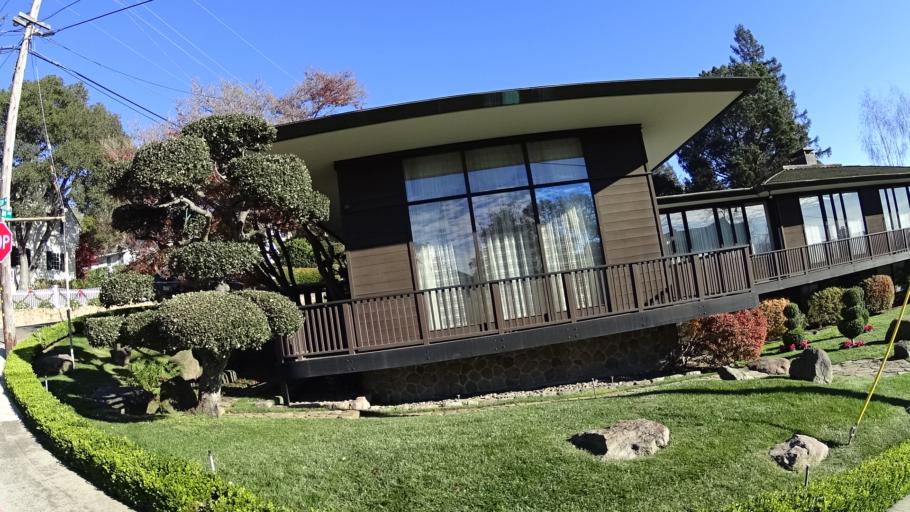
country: US
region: California
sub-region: Alameda County
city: Piedmont
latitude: 37.8231
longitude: -122.2269
